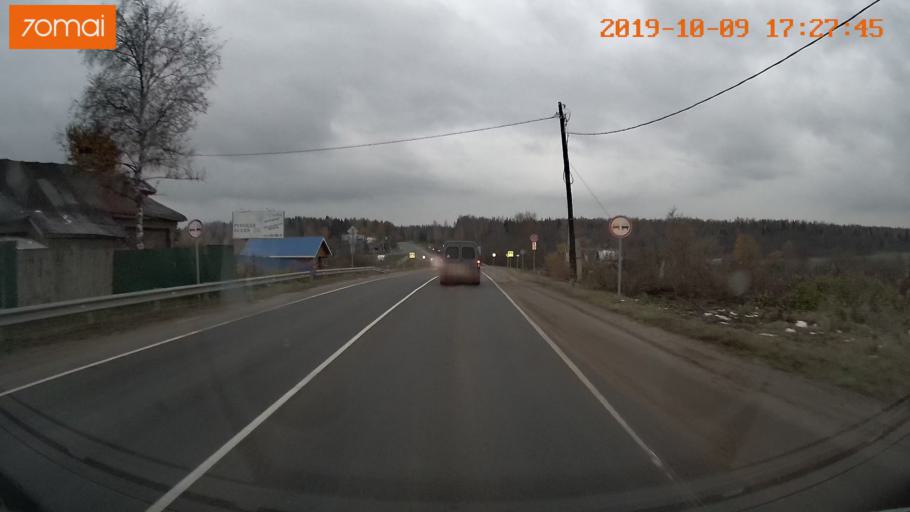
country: RU
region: Ivanovo
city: Furmanov
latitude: 57.1639
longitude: 41.0698
